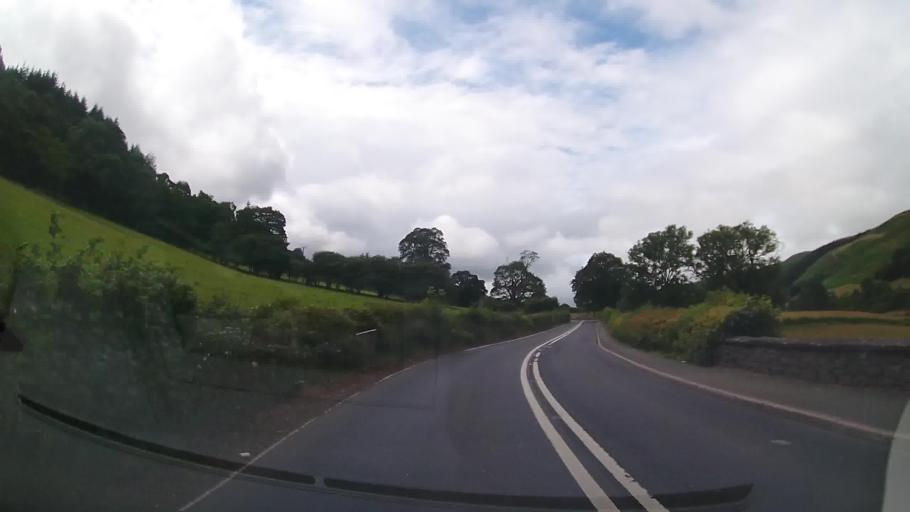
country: GB
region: Wales
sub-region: Denbighshire
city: Bryneglwys
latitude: 52.9758
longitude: -3.2826
